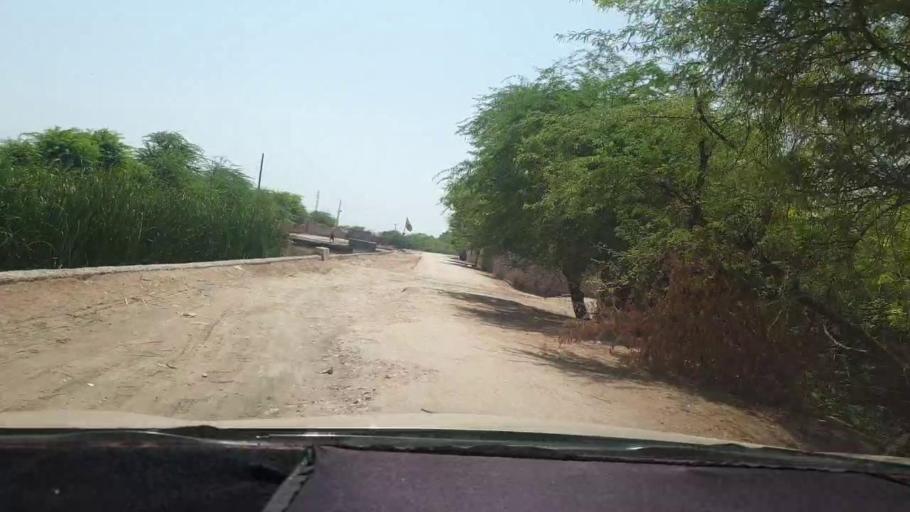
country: PK
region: Sindh
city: Shahdadkot
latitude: 27.8360
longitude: 67.9389
